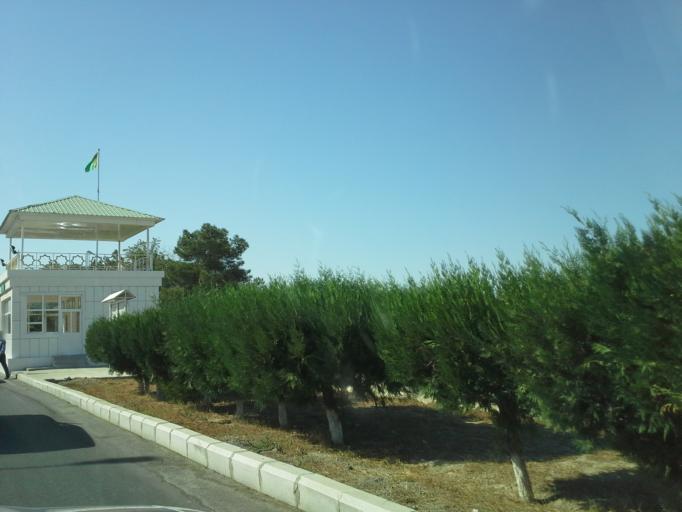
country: TM
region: Ahal
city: Ashgabat
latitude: 37.9204
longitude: 58.4484
